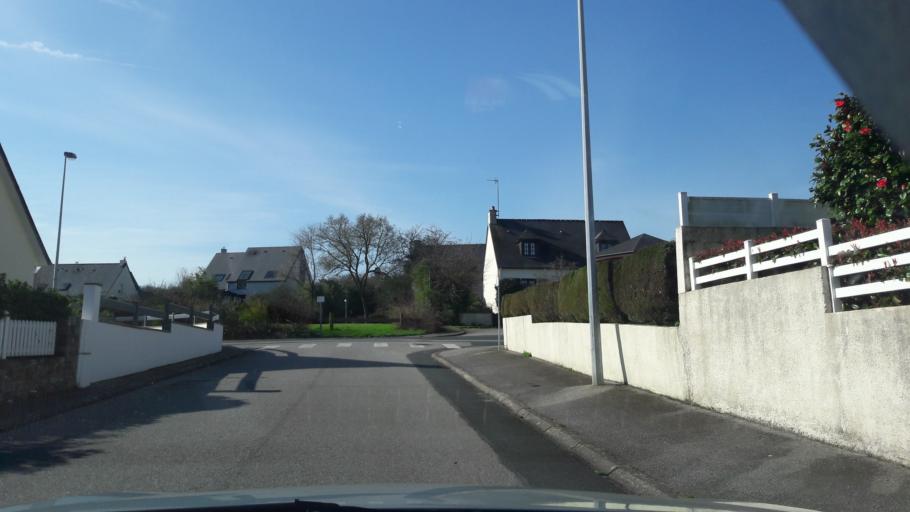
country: FR
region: Lower Normandy
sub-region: Departement de la Manche
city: Querqueville
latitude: 49.6572
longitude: -1.6849
